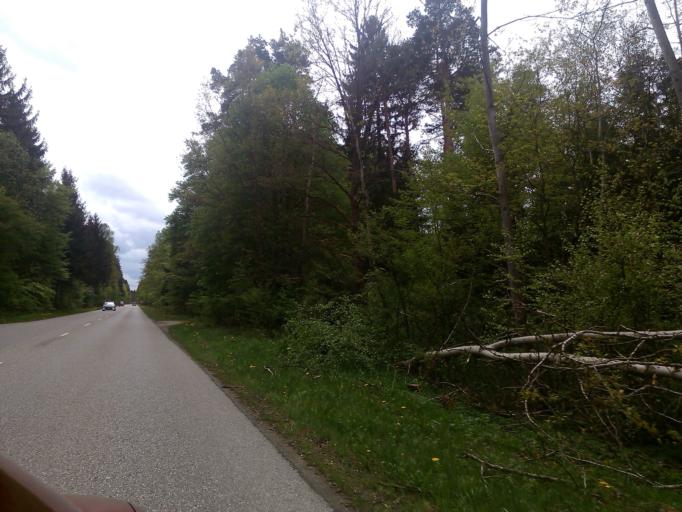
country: DE
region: Bavaria
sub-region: Upper Bavaria
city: Krailling
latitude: 48.1065
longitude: 11.3742
